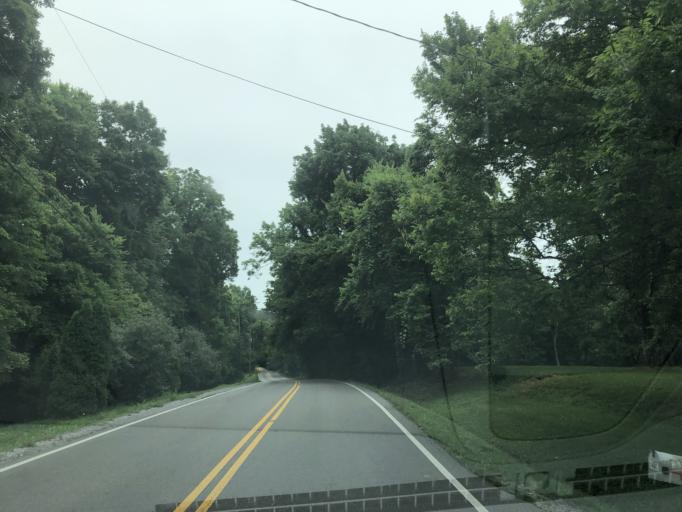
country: US
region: Tennessee
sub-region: Williamson County
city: Nolensville
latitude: 36.0341
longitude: -86.6861
